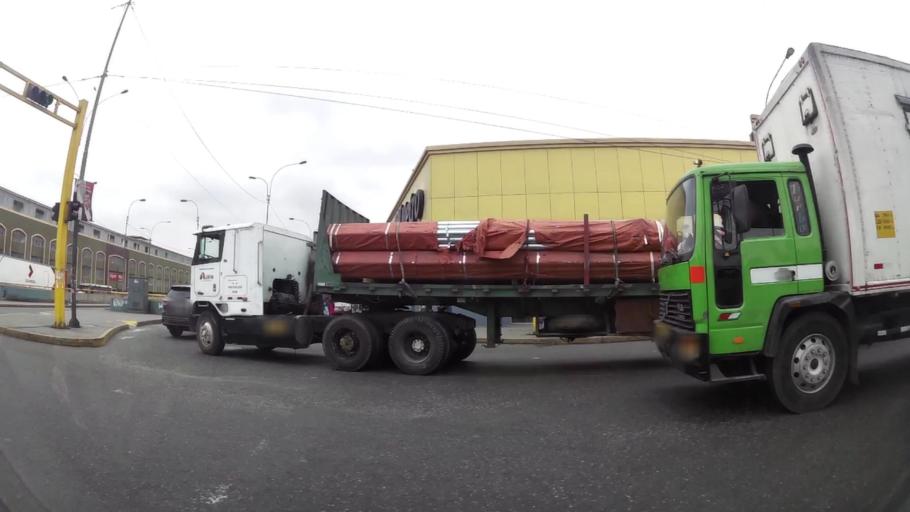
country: PE
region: Lima
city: Lima
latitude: -12.0428
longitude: -77.0428
